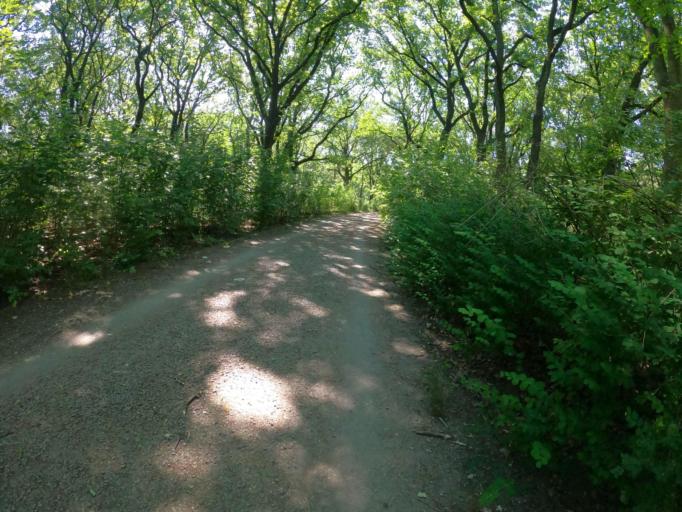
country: DE
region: Berlin
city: Charlottenburg-Nord
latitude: 52.5461
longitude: 13.2945
